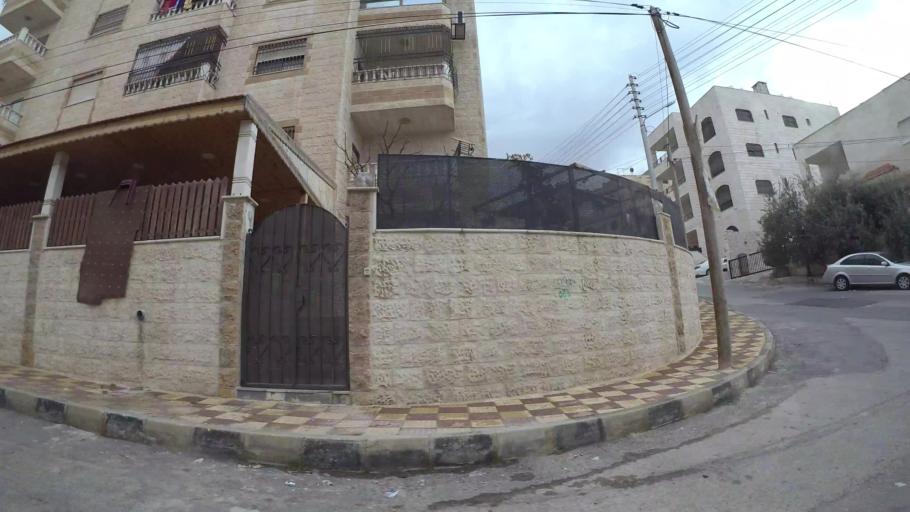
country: JO
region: Amman
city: Amman
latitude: 32.0060
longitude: 35.9469
